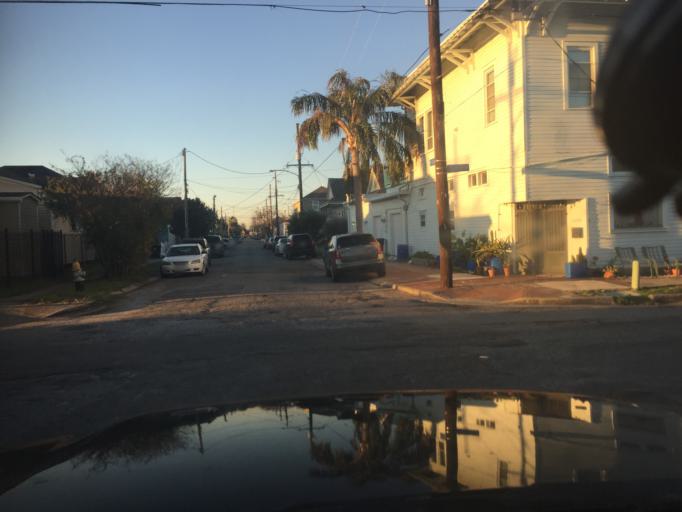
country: US
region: Louisiana
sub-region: Orleans Parish
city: New Orleans
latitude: 29.9753
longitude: -90.0861
